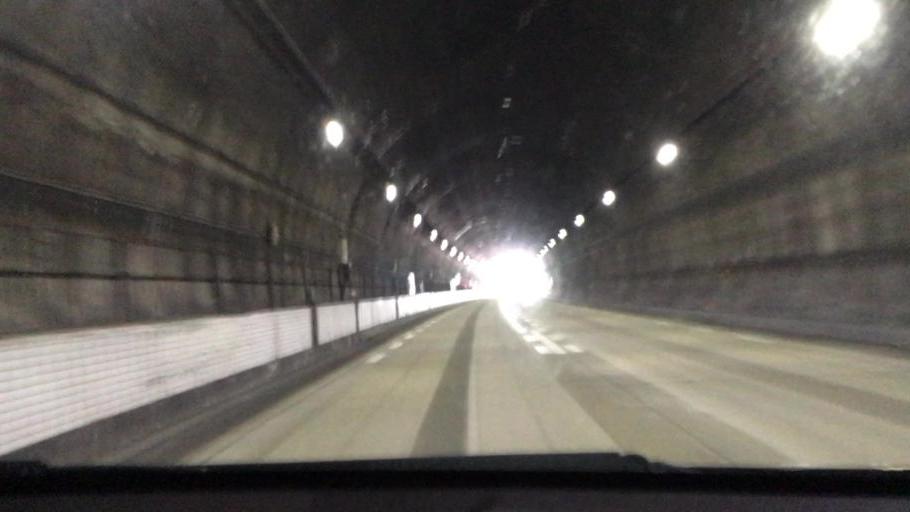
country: JP
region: Yamaguchi
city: Hofu
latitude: 34.0562
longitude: 131.6199
